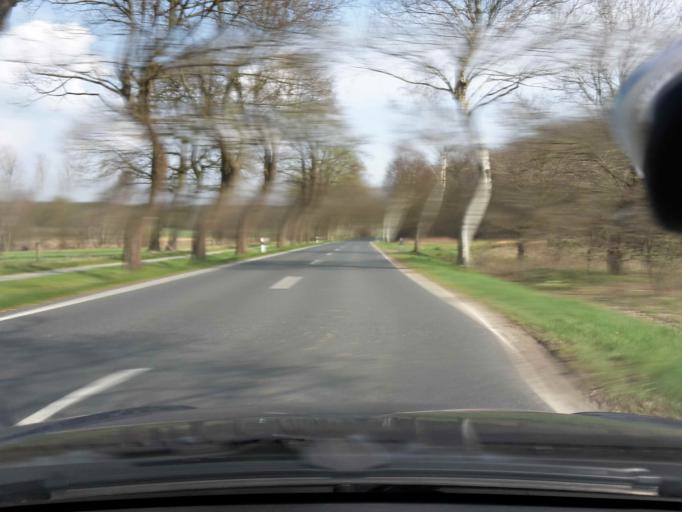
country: DE
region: Lower Saxony
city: Jesteburg
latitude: 53.3008
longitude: 9.9349
